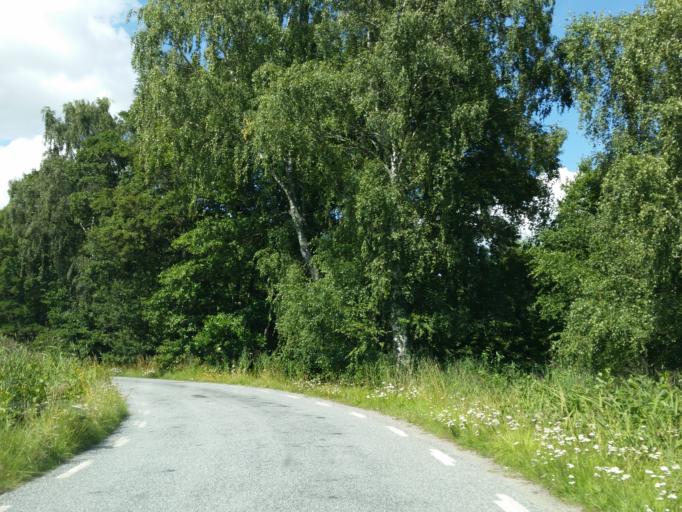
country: SE
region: Stockholm
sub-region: Sodertalje Kommun
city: Pershagen
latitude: 59.0435
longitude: 17.6617
